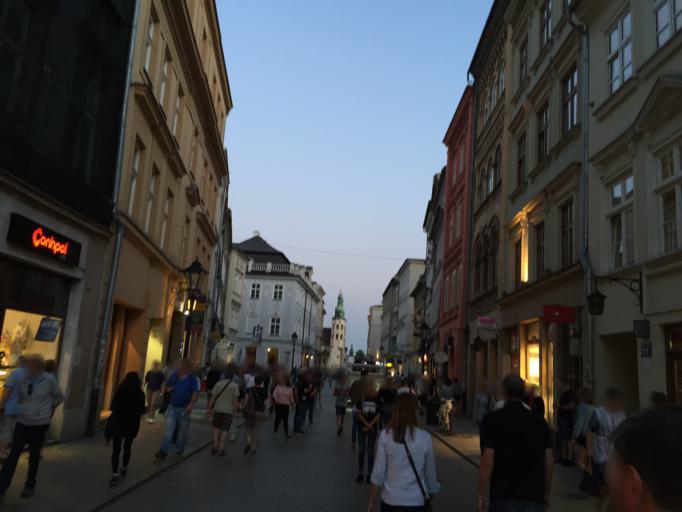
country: PL
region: Lesser Poland Voivodeship
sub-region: Krakow
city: Krakow
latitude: 50.0588
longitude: 19.9379
